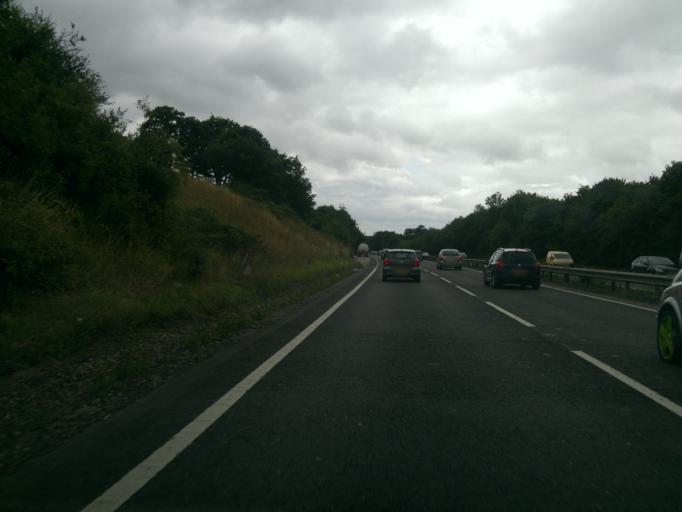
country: GB
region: England
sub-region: Essex
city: Great Horkesley
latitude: 51.9164
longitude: 0.8754
